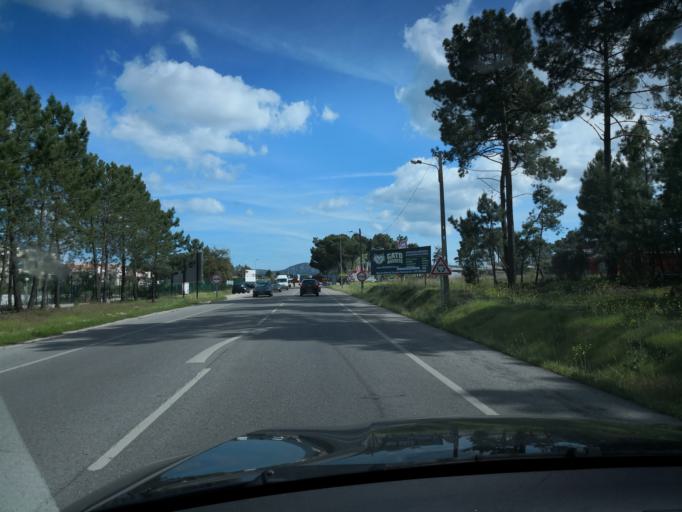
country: PT
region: Setubal
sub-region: Barreiro
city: Santo Antonio da Charneca
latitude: 38.5467
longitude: -9.0303
